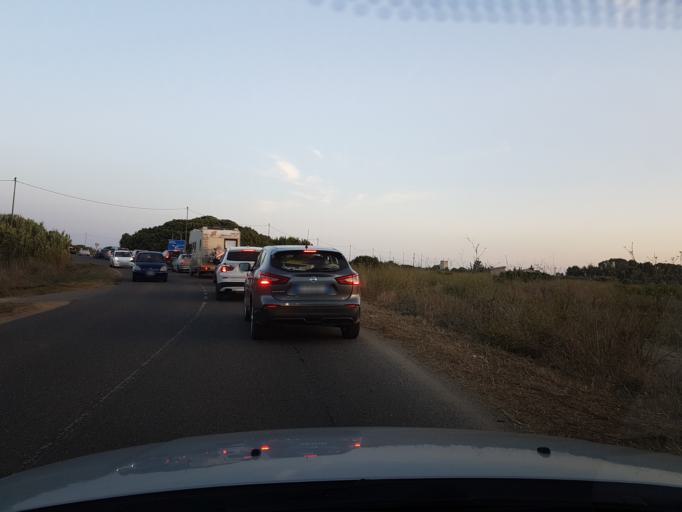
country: IT
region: Sardinia
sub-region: Provincia di Oristano
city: Cabras
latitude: 39.9180
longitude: 8.4512
